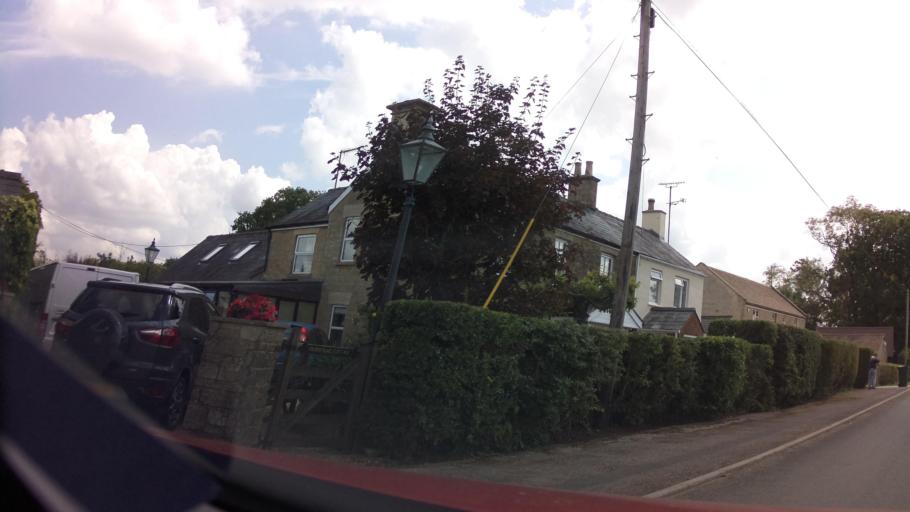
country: GB
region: England
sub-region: Wiltshire
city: Minety
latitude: 51.6115
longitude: -1.9826
